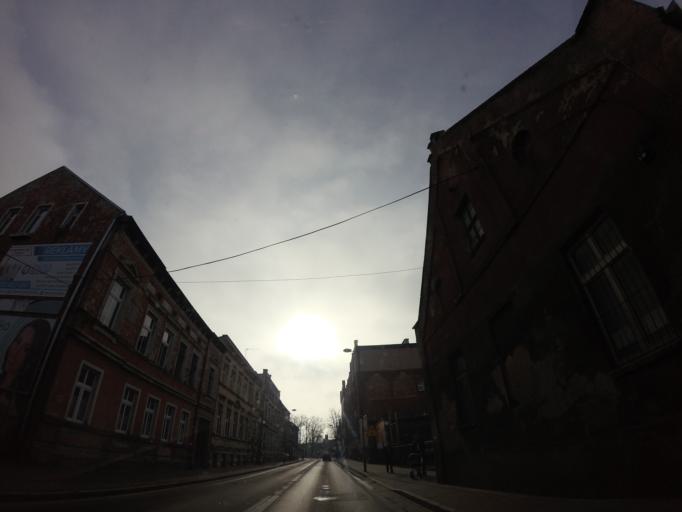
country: PL
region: West Pomeranian Voivodeship
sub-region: Powiat walecki
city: Walcz
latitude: 53.2738
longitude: 16.4663
